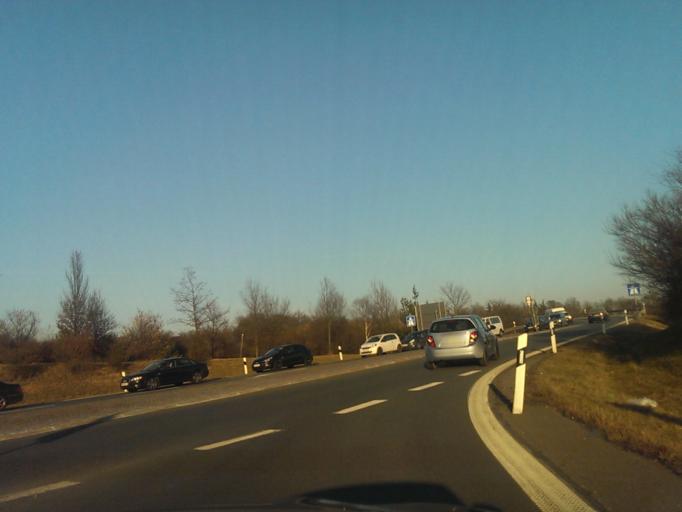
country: DE
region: Saxony
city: Weischlitz
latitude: 50.4345
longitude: 12.0908
